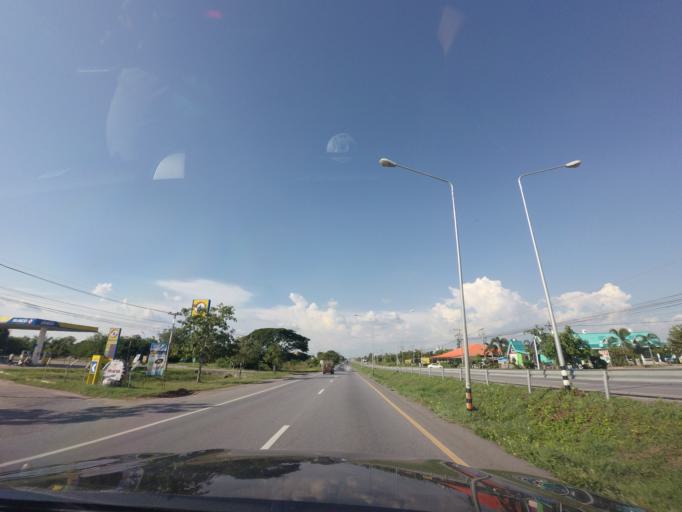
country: TH
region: Khon Kaen
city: Non Sila
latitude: 15.9792
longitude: 102.6953
